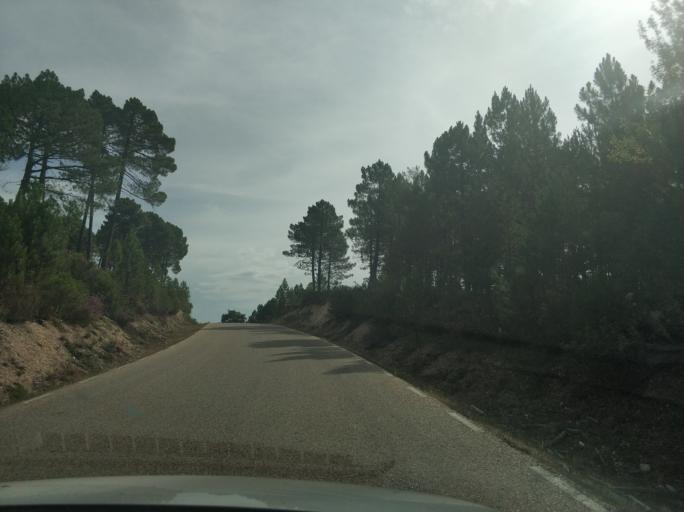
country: ES
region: Castille and Leon
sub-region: Provincia de Soria
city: Navaleno
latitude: 41.8505
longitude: -2.9832
